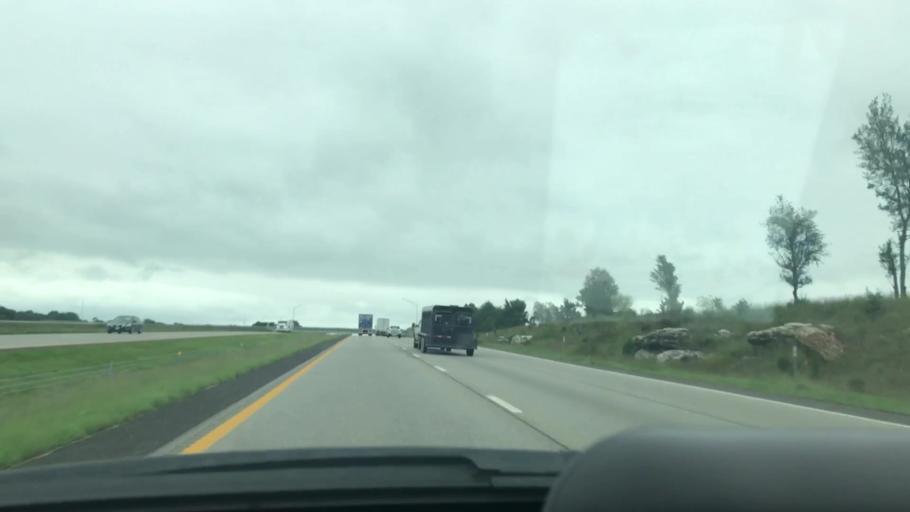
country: US
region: Missouri
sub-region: Greene County
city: Republic
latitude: 37.1948
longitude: -93.4502
